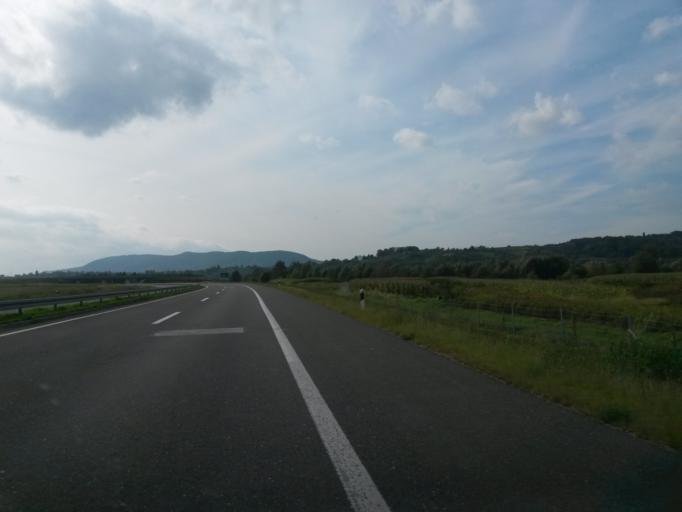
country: HR
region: Varazdinska
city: Ljubescica
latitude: 46.1793
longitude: 16.3869
